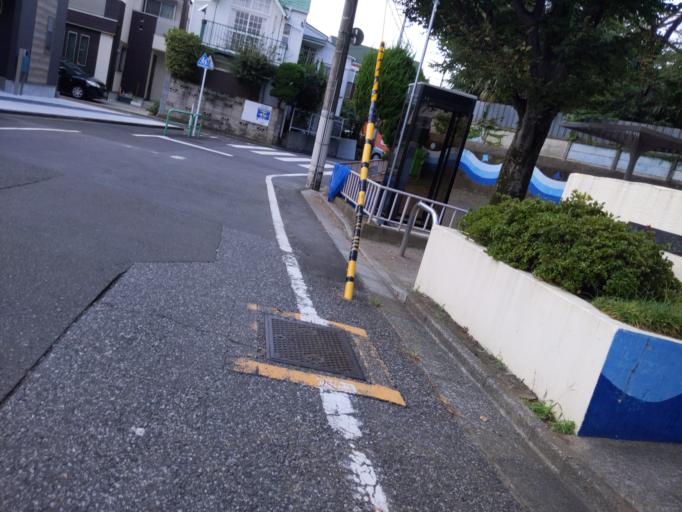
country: JP
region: Saitama
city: Wako
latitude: 35.7459
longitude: 139.6411
